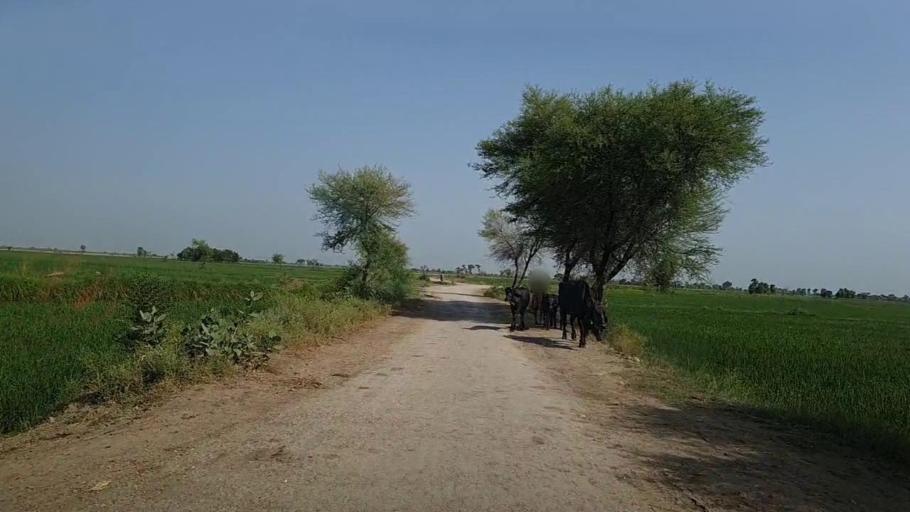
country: PK
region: Sindh
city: Sita Road
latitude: 27.1071
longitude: 67.8498
